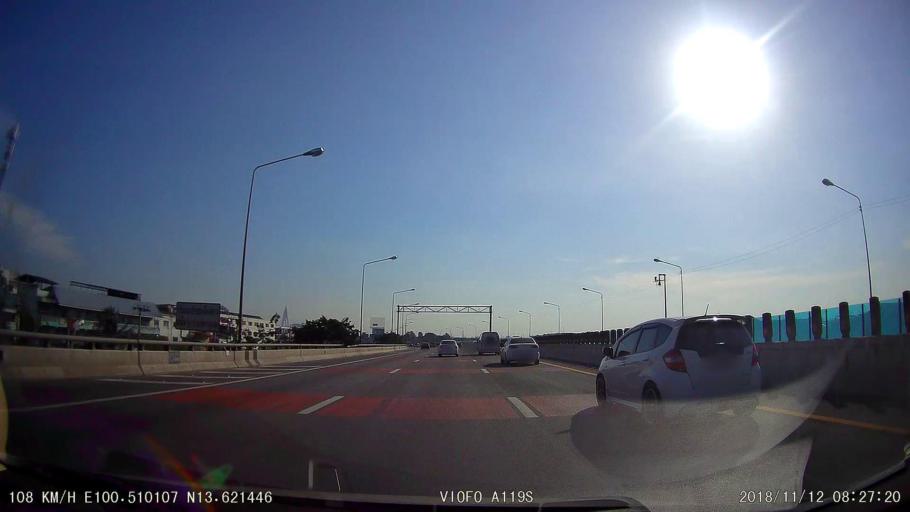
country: TH
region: Bangkok
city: Thung Khru
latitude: 13.6216
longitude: 100.5115
